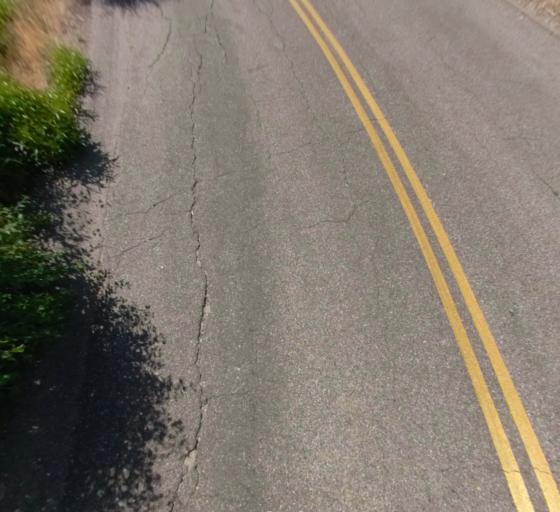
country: US
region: California
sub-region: Fresno County
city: Auberry
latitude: 37.2652
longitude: -119.3582
